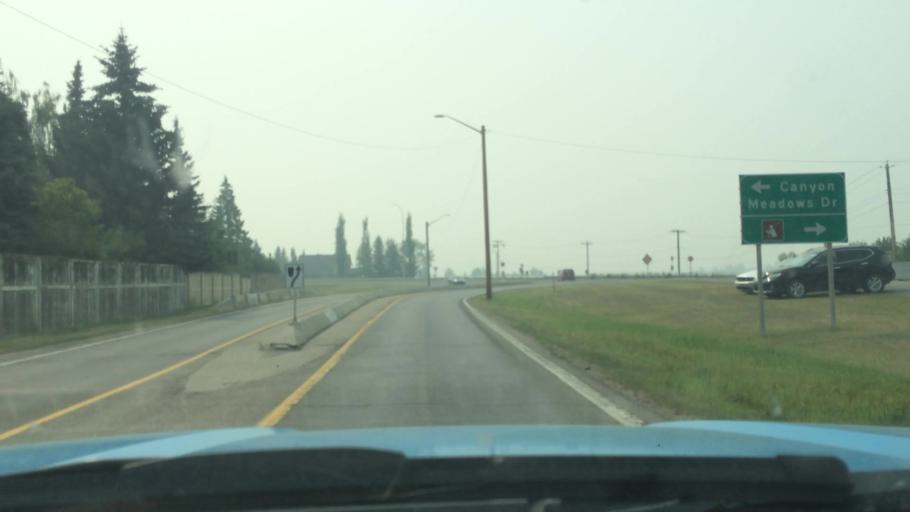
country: CA
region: Alberta
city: Calgary
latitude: 50.9416
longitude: -114.0944
